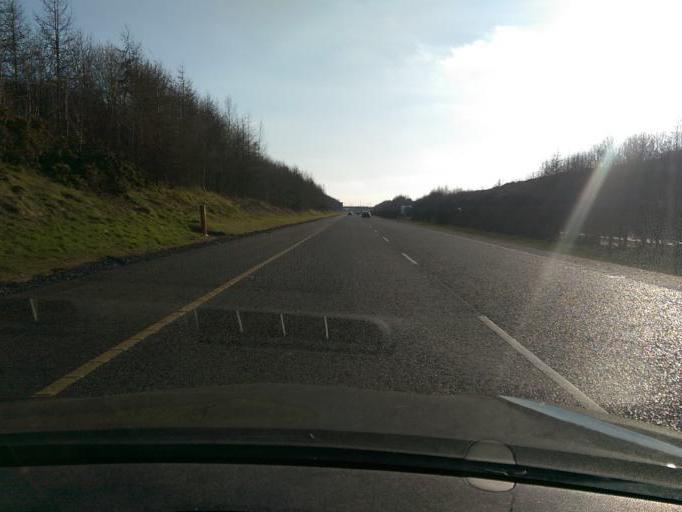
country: IE
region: Leinster
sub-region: Laois
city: Stradbally
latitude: 53.0666
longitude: -7.2172
